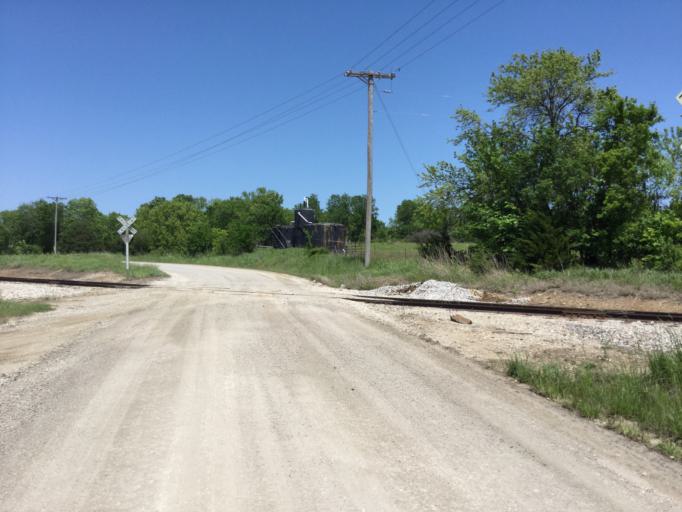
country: US
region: Kansas
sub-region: Montgomery County
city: Cherryvale
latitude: 37.2277
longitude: -95.4462
